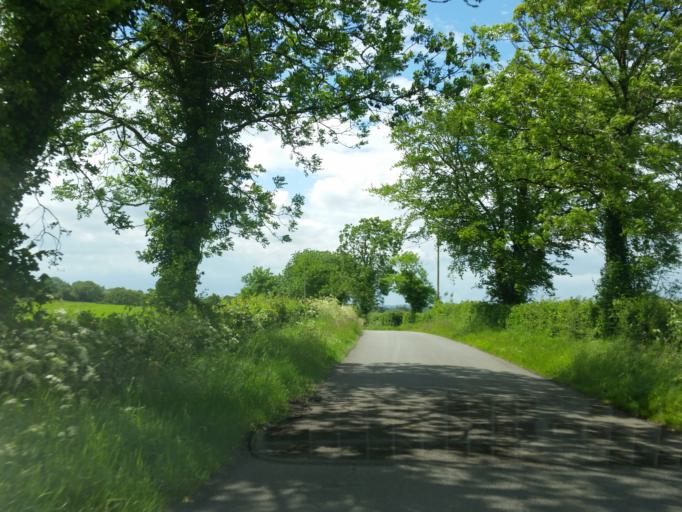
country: GB
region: Northern Ireland
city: Fivemiletown
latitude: 54.3673
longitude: -7.2798
